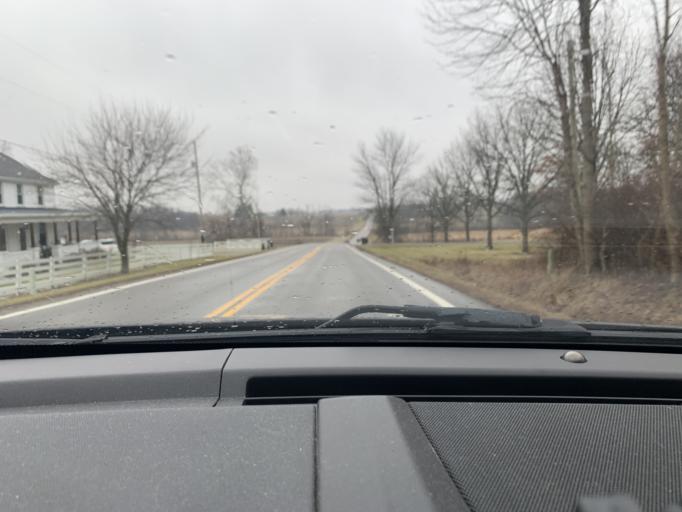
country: US
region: Ohio
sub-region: Ross County
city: Kingston
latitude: 39.4342
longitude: -82.8947
